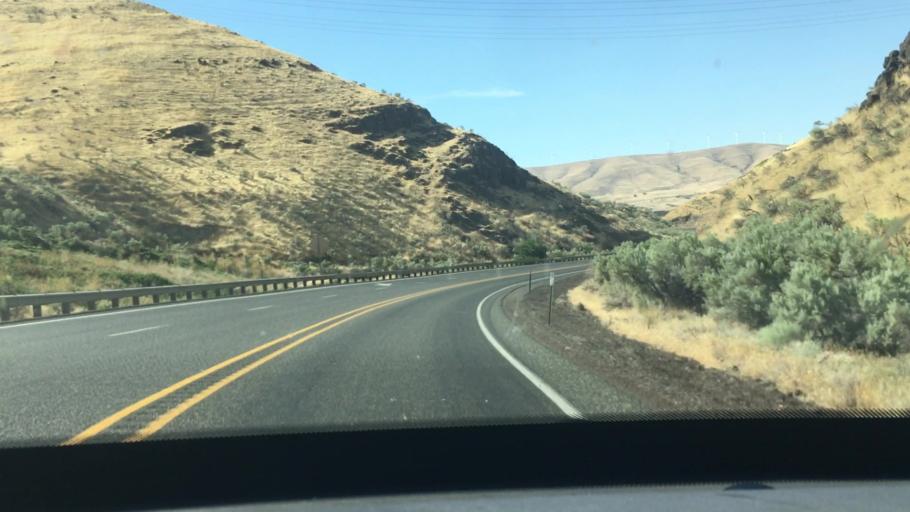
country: US
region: Washington
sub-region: Klickitat County
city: Goldendale
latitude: 45.6506
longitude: -120.8153
